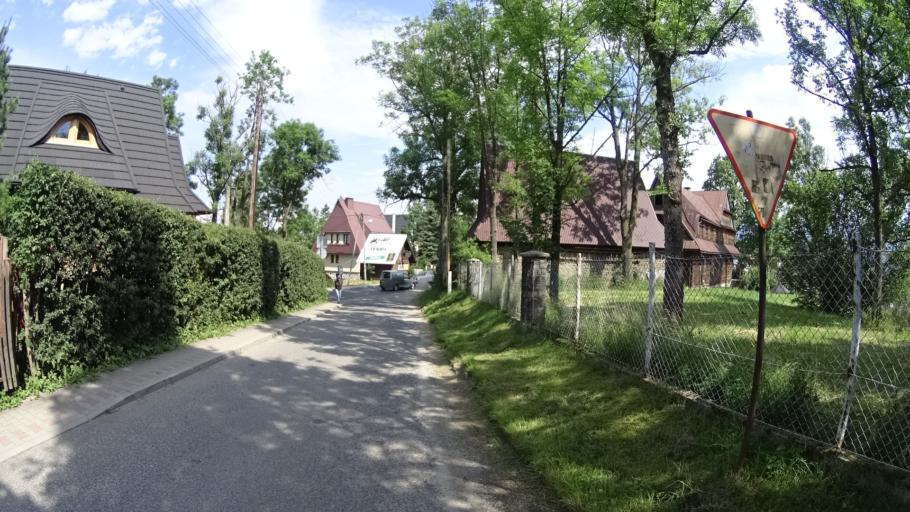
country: PL
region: Lesser Poland Voivodeship
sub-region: Powiat tatrzanski
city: Bukowina Tatrzanska
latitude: 49.3329
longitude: 20.0919
